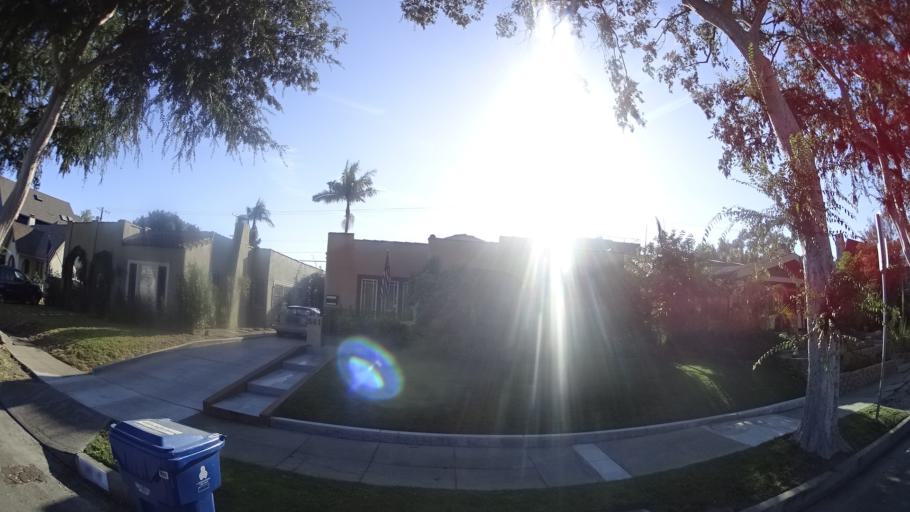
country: US
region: California
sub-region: Los Angeles County
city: Hollywood
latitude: 34.0807
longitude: -118.3227
